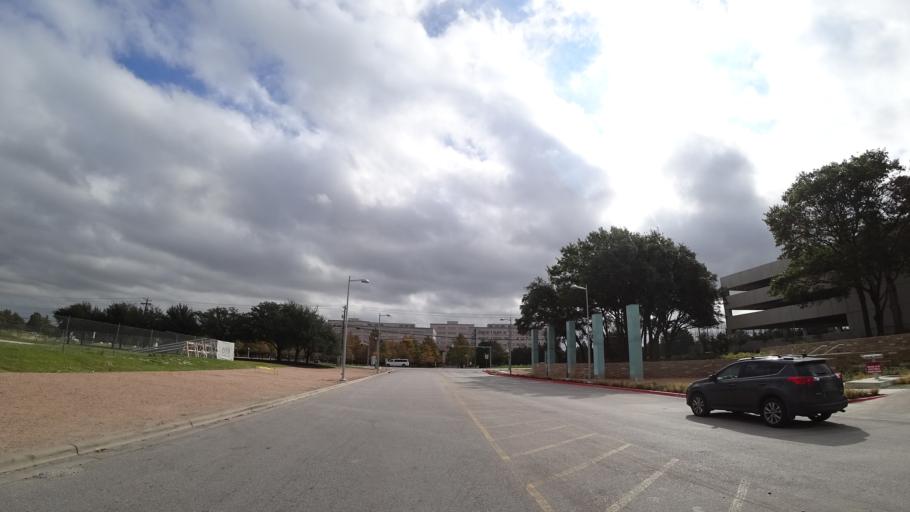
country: US
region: Texas
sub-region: Travis County
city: Wells Branch
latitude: 30.4026
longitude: -97.7185
